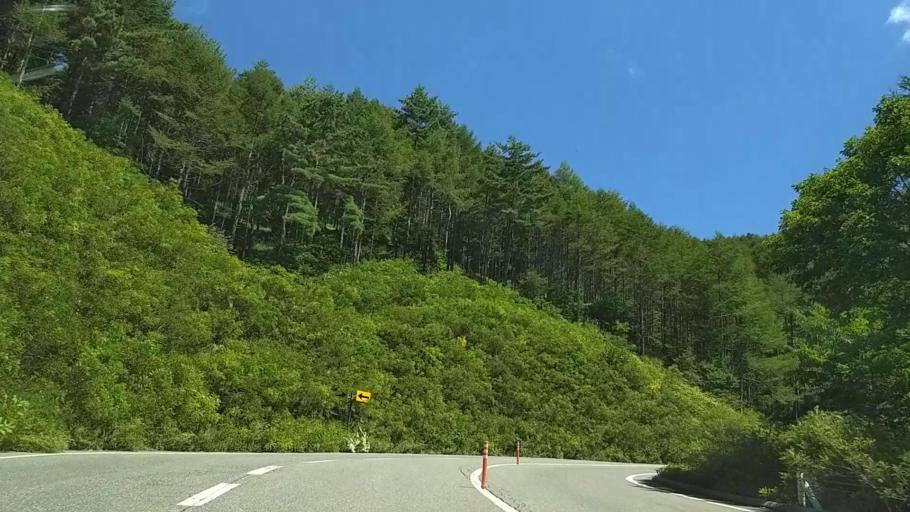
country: JP
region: Nagano
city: Suwa
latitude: 36.1137
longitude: 138.2350
